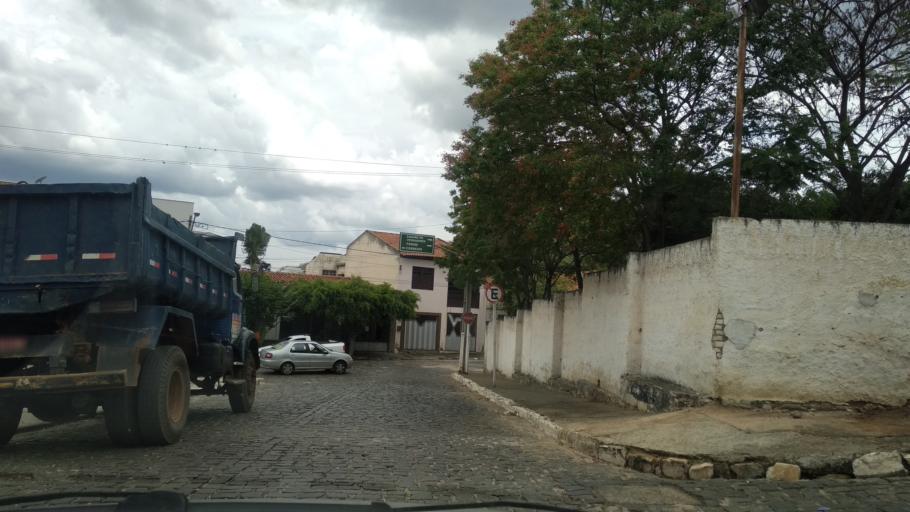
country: BR
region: Bahia
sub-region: Caetite
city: Caetite
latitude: -14.0695
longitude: -42.4845
